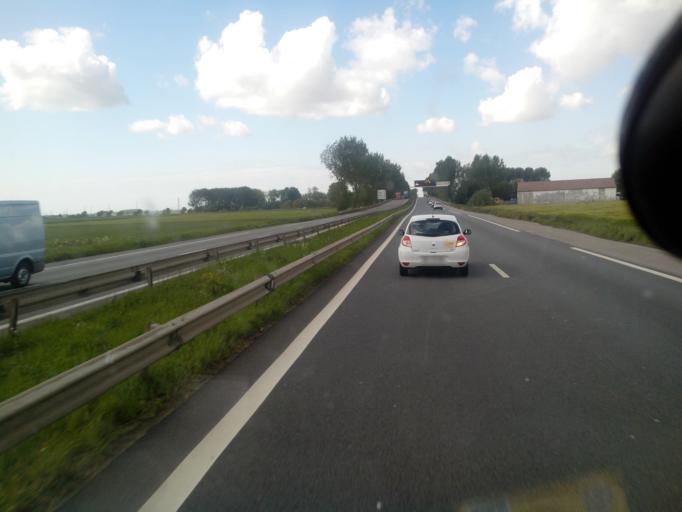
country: FR
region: Nord-Pas-de-Calais
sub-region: Departement du Nord
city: Bierne
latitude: 50.9657
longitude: 2.3994
